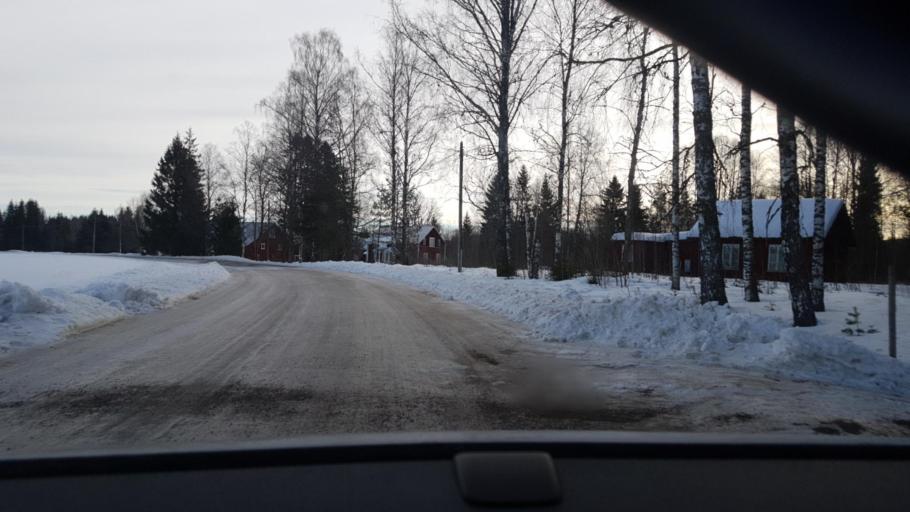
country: SE
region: Vaermland
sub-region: Eda Kommun
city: Amotfors
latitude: 59.7244
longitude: 12.1660
